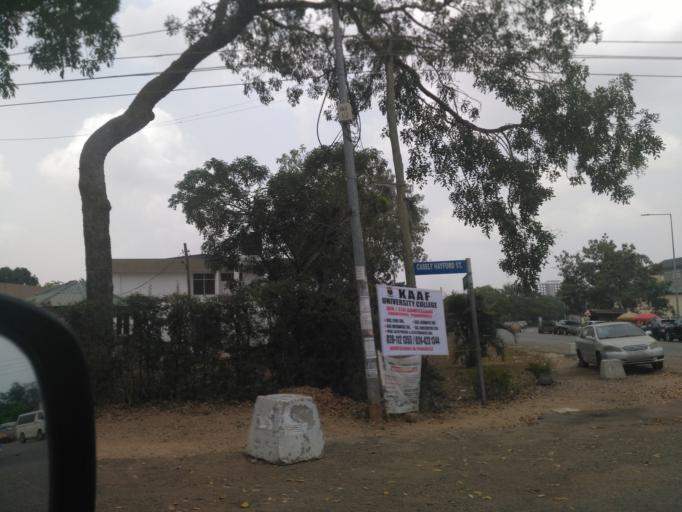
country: GH
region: Greater Accra
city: Accra
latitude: 5.5956
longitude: -0.1820
